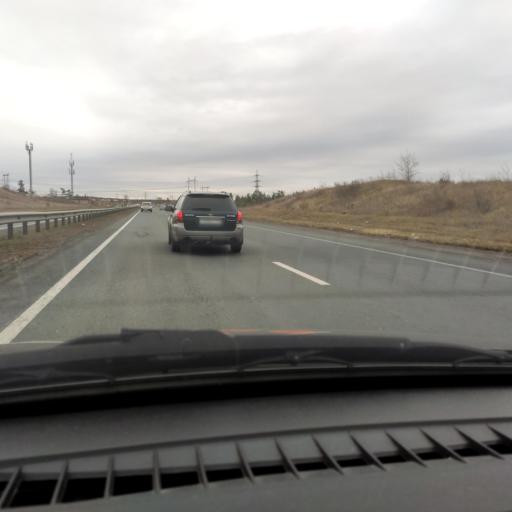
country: RU
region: Samara
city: Zhigulevsk
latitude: 53.5238
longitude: 49.5279
